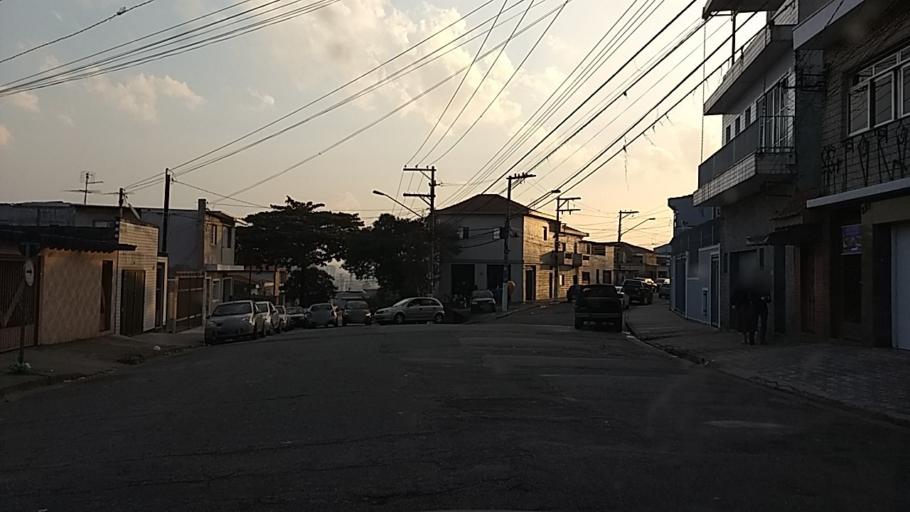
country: BR
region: Sao Paulo
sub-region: Sao Paulo
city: Sao Paulo
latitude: -23.5072
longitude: -46.5903
